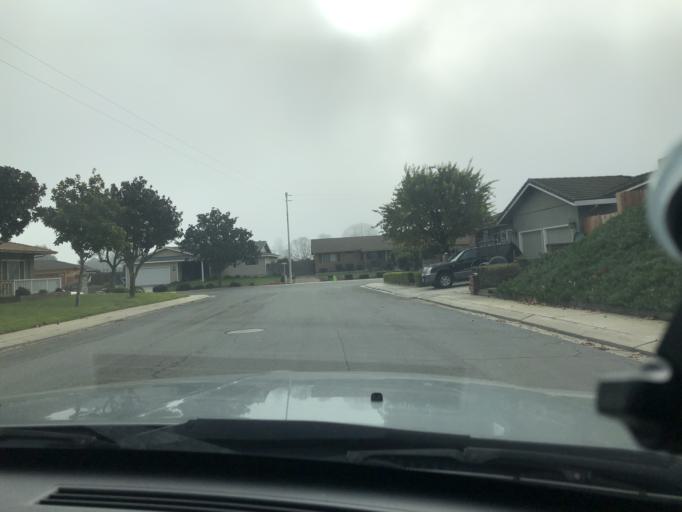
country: US
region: California
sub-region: Monterey County
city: King City
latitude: 36.2086
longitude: -121.1212
